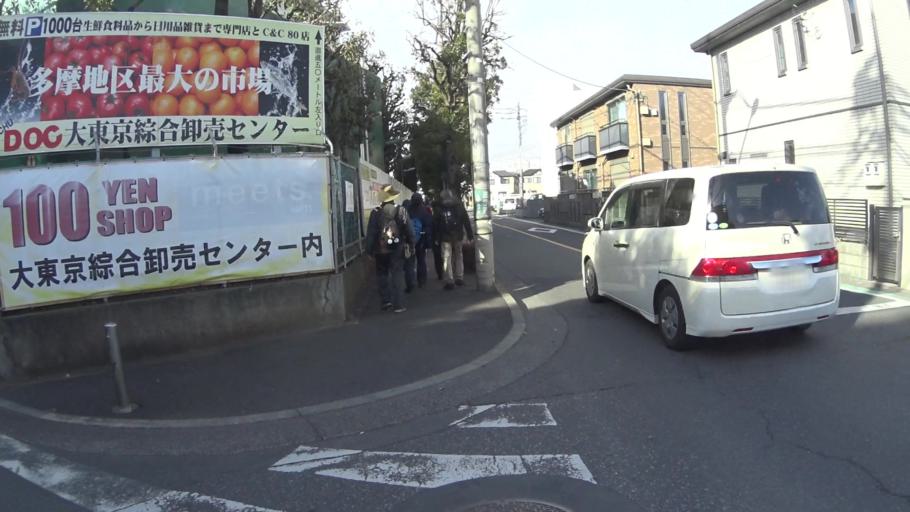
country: JP
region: Tokyo
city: Kokubunji
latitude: 35.6581
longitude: 139.4803
